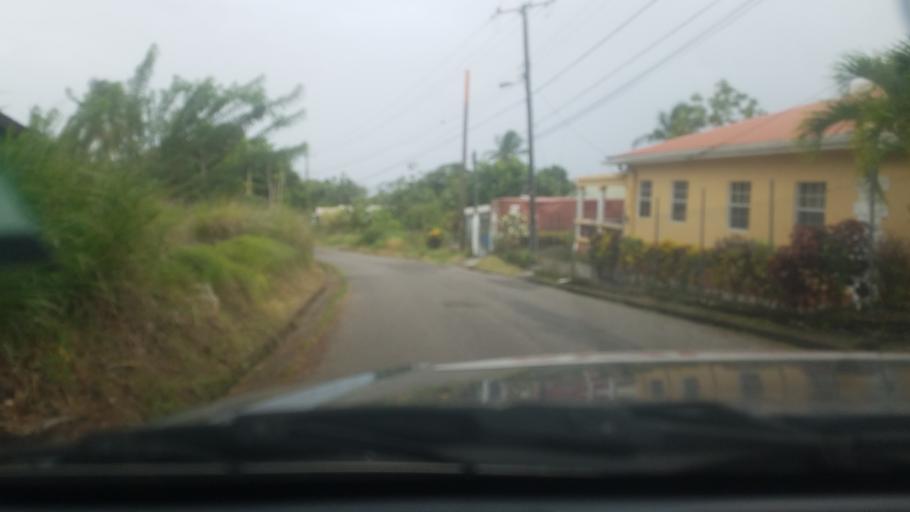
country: LC
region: Laborie Quarter
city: Laborie
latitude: 13.7585
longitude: -60.9806
